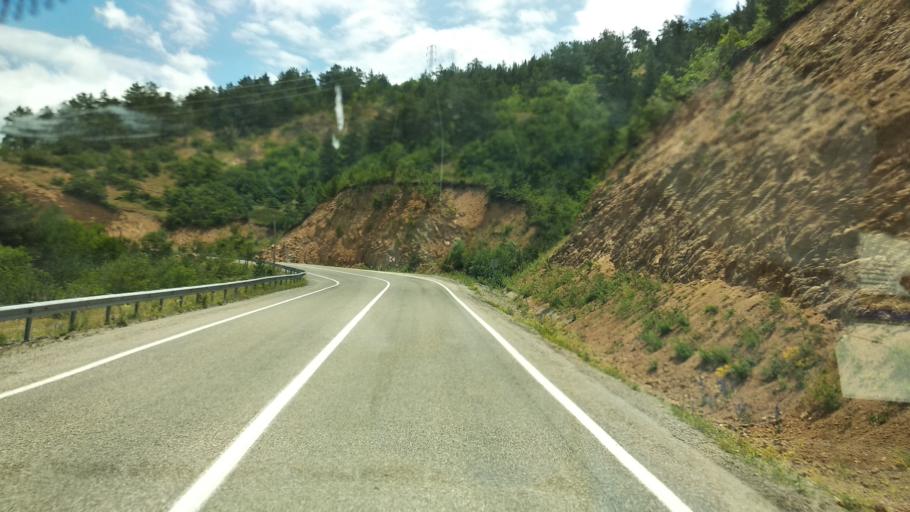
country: TR
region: Gumushane
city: Kose
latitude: 40.2985
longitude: 39.5662
